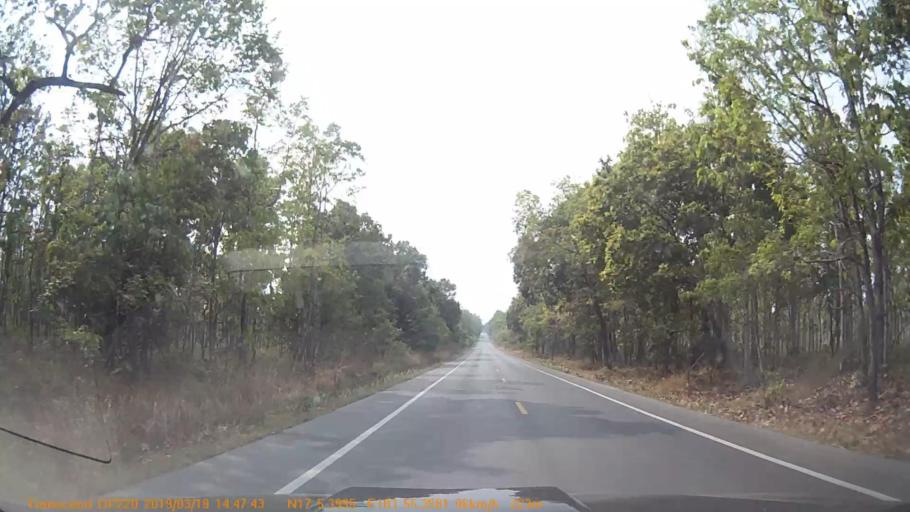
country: TH
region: Sakon Nakhon
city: Kut Bak
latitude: 17.0902
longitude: 103.9224
